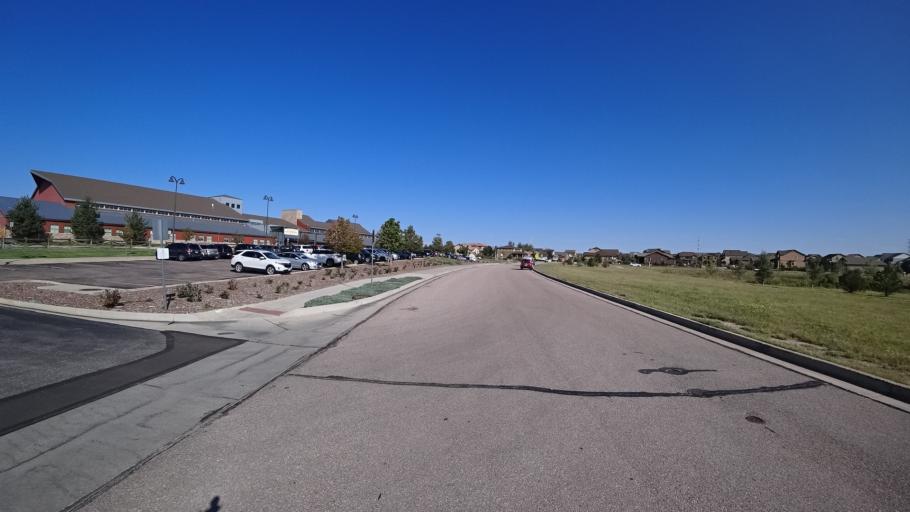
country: US
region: Colorado
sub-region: El Paso County
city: Cimarron Hills
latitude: 38.9332
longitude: -104.6740
